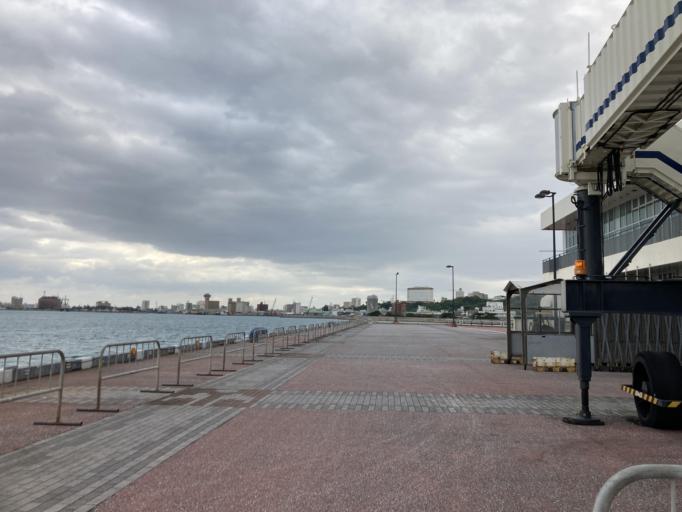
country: JP
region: Okinawa
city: Naha-shi
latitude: 26.2257
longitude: 127.6745
